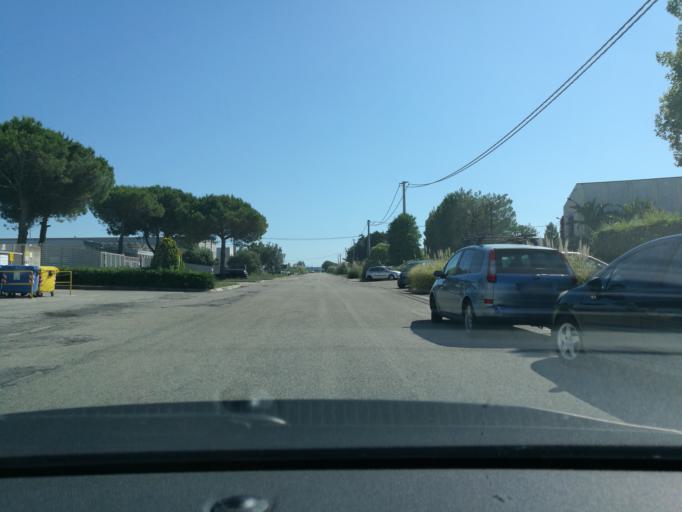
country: IT
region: Abruzzo
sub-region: Provincia di Chieti
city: Vasto
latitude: 42.1723
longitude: 14.6971
